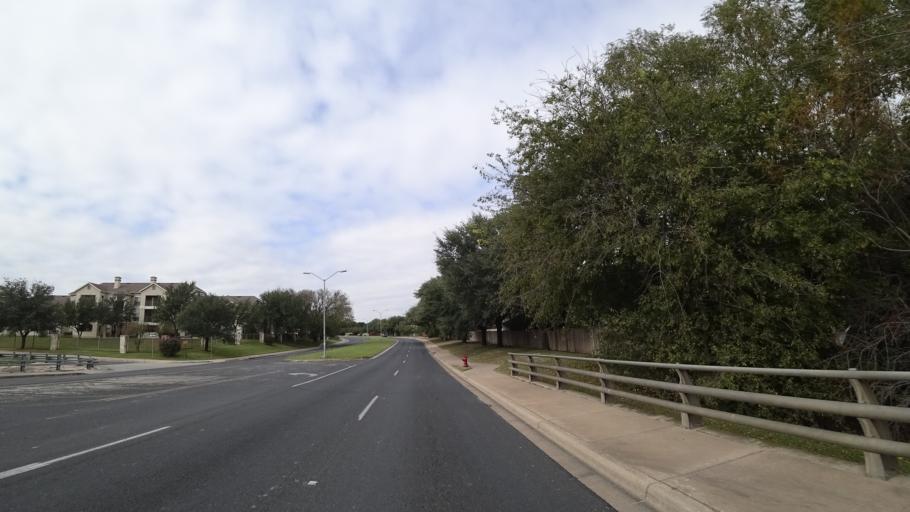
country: US
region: Texas
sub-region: Travis County
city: Windemere
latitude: 30.4566
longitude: -97.6546
